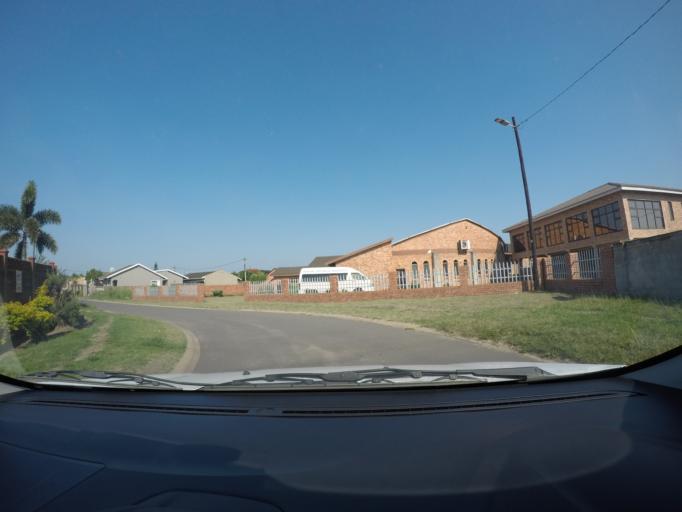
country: ZA
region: KwaZulu-Natal
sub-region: uThungulu District Municipality
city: Richards Bay
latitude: -28.7214
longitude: 32.0362
